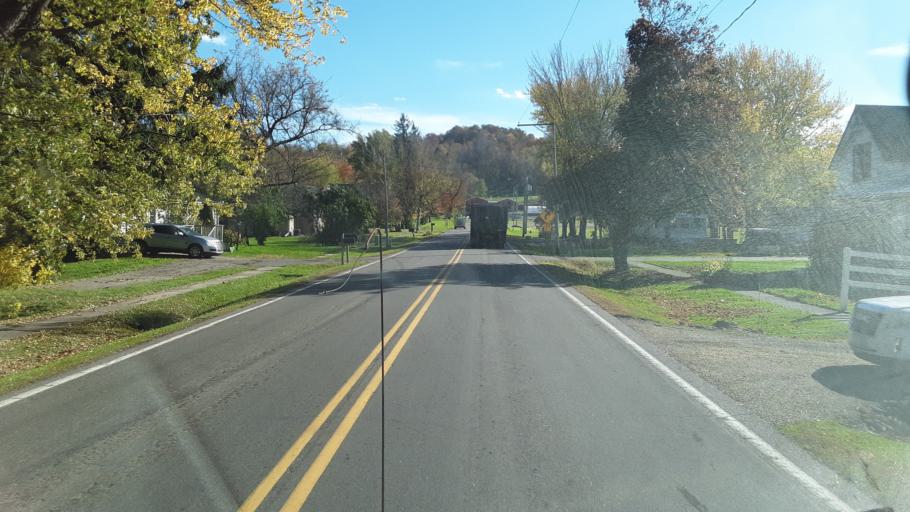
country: US
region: Wisconsin
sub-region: Sauk County
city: Reedsburg
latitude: 43.5431
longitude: -90.1413
